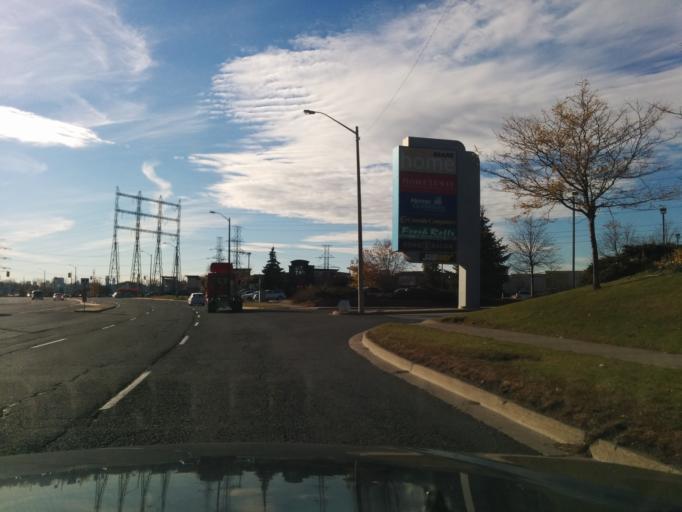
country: CA
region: Ontario
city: Etobicoke
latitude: 43.6143
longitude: -79.5583
